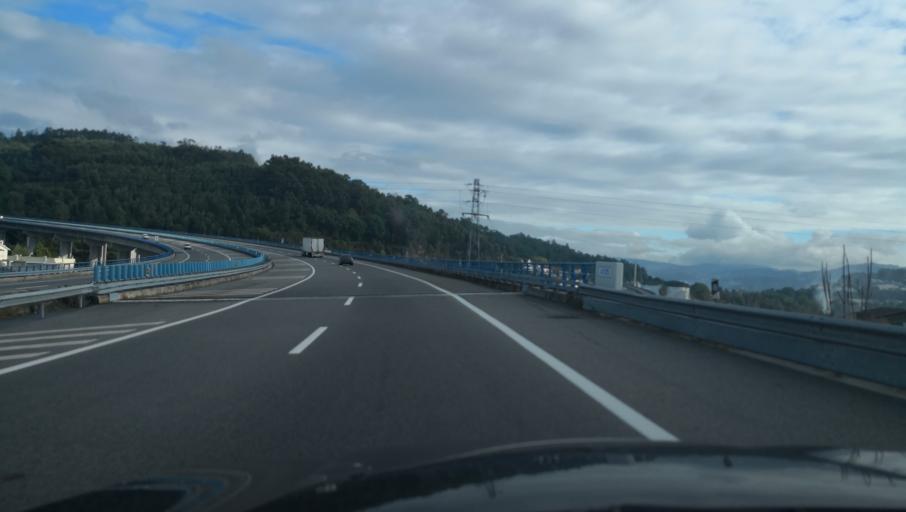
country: PT
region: Braga
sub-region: Guimaraes
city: Candoso
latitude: 41.4109
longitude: -8.3234
